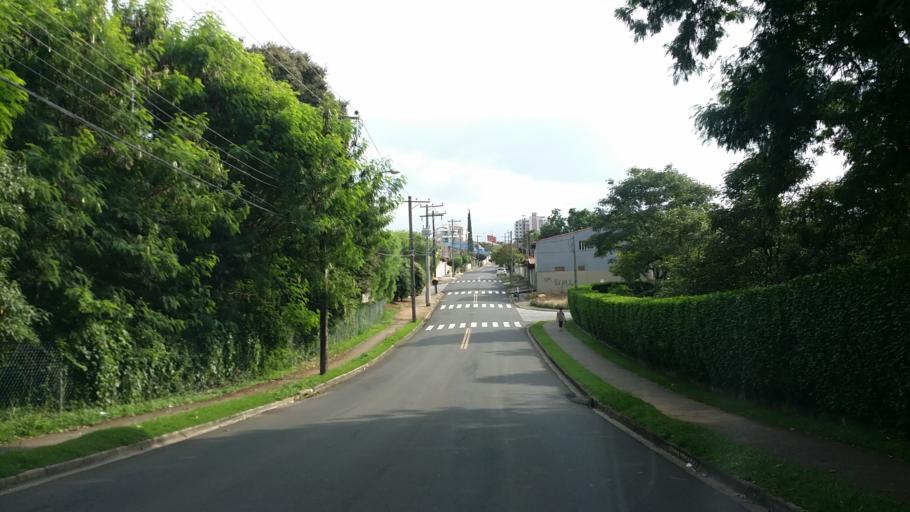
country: BR
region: Sao Paulo
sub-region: Indaiatuba
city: Indaiatuba
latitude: -23.0973
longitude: -47.2035
